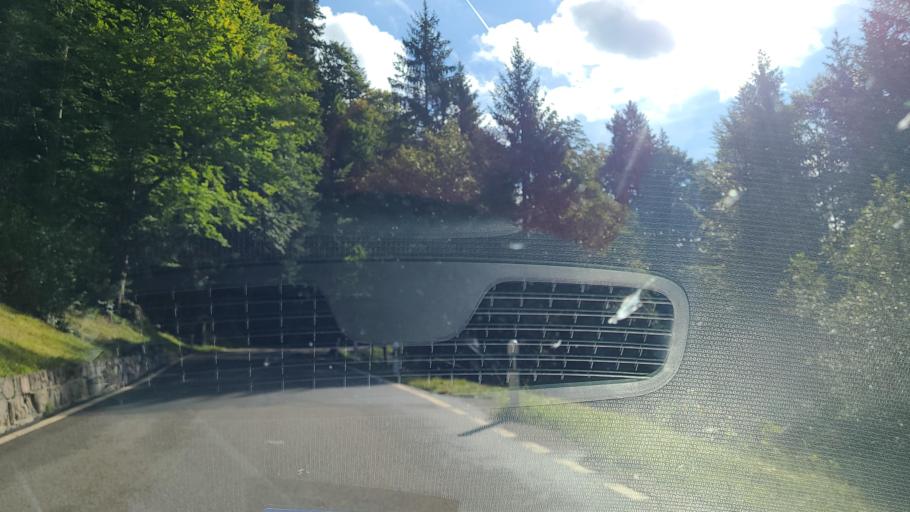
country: CH
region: Schwyz
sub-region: Bezirk March
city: Altendorf
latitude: 47.1305
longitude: 8.8299
